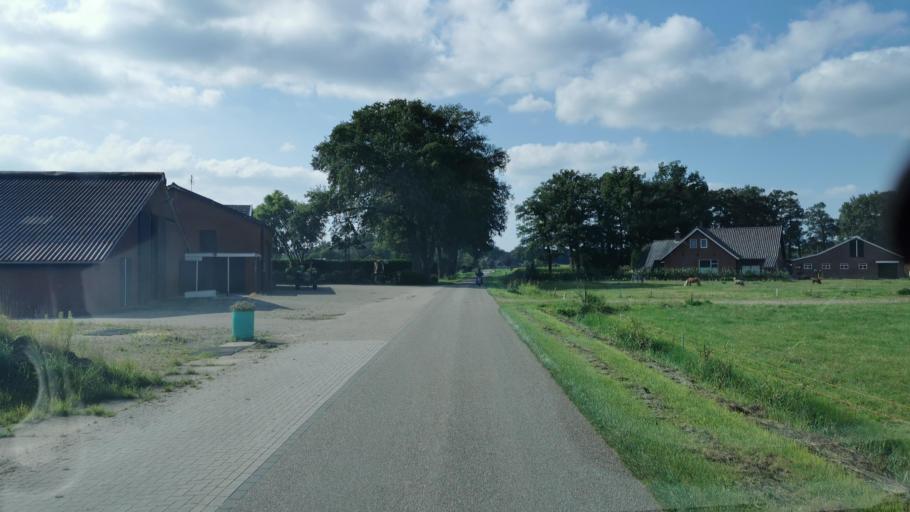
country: NL
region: Overijssel
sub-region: Gemeente Hengelo
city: Hengelo
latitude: 52.3216
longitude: 6.8073
